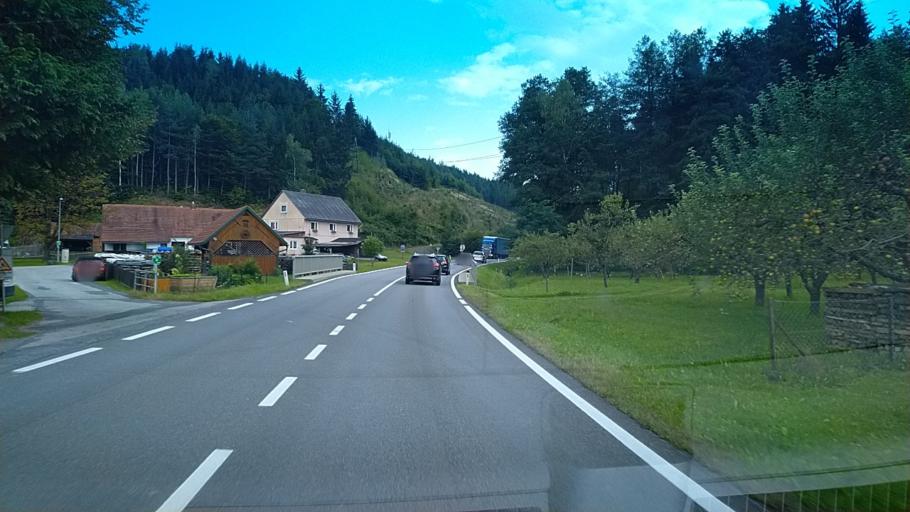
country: AT
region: Styria
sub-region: Politischer Bezirk Deutschlandsberg
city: Schwanberg
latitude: 46.7498
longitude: 15.2277
